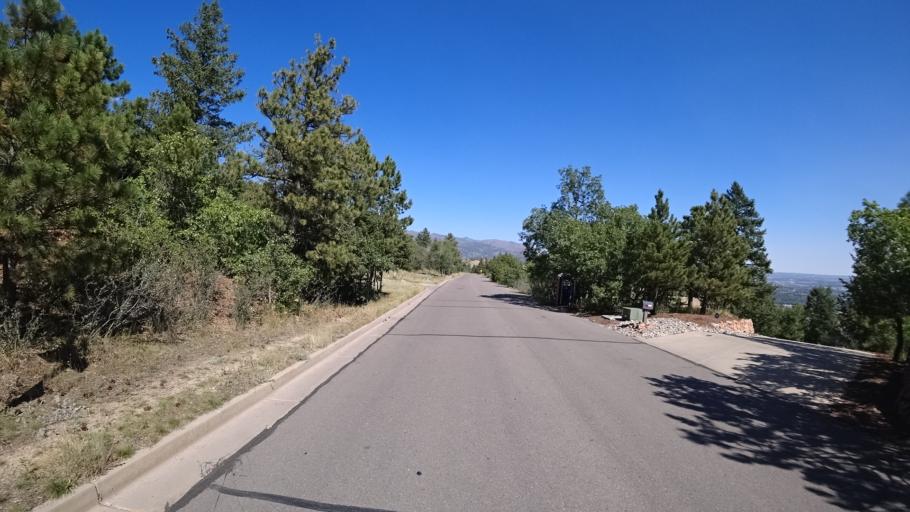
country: US
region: Colorado
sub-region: El Paso County
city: Manitou Springs
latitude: 38.8144
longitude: -104.8807
